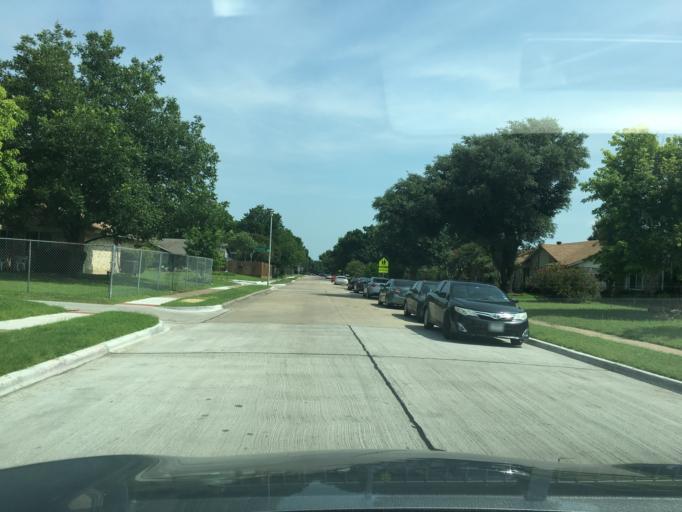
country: US
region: Texas
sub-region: Dallas County
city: Garland
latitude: 32.9260
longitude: -96.6715
